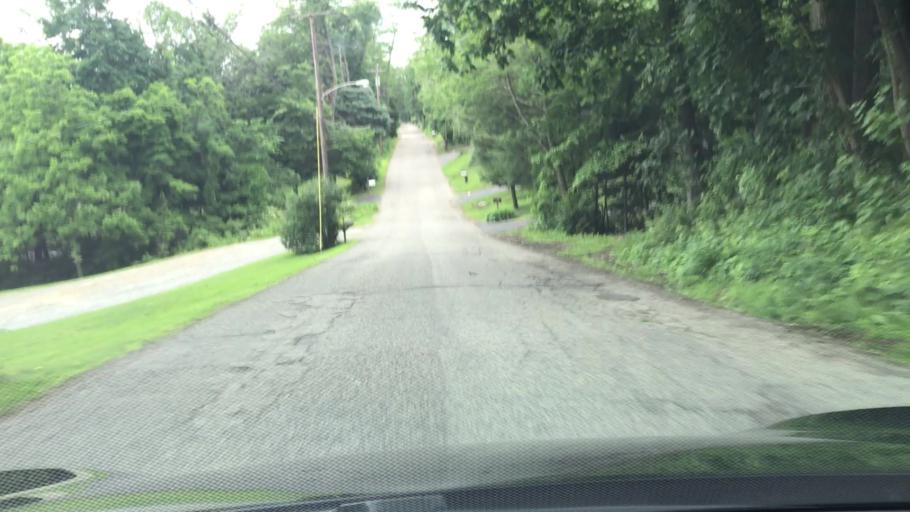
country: US
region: New Jersey
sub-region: Hunterdon County
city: Lebanon
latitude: 40.6333
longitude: -74.8238
